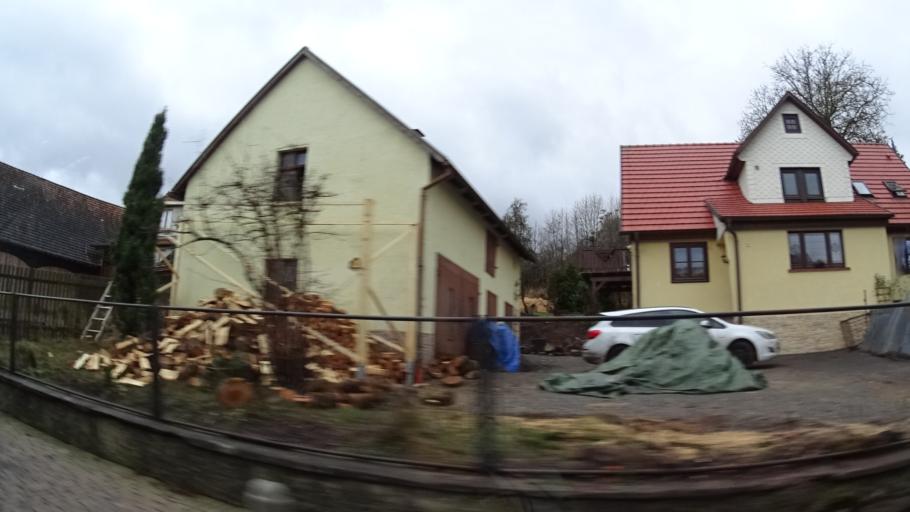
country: DE
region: Thuringia
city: Stepfershausen
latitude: 50.5945
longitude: 10.3014
